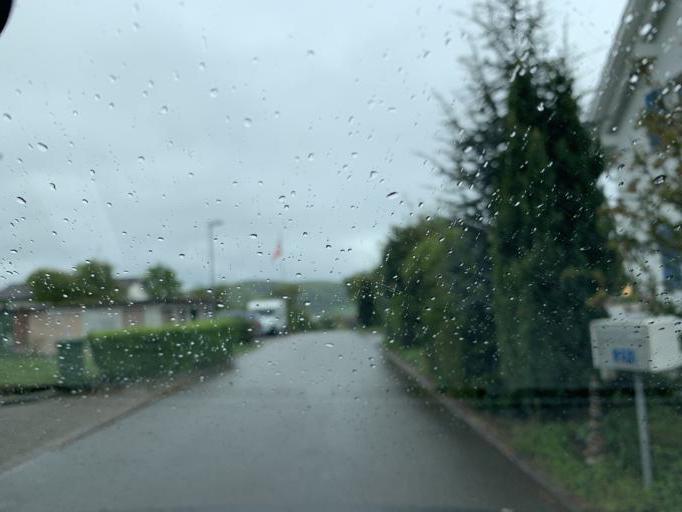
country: CH
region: Schaffhausen
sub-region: Bezirk Schaffhausen
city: Beringen
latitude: 47.7009
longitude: 8.5708
